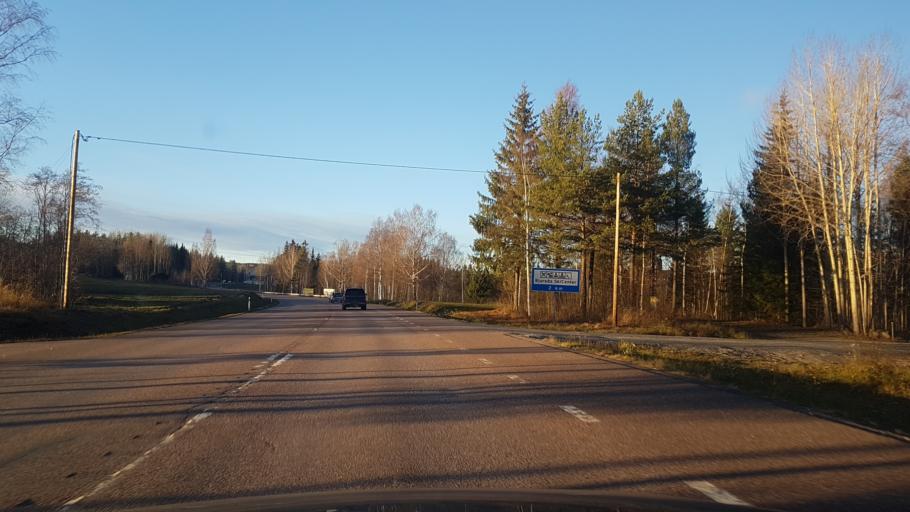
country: SE
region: Dalarna
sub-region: Faluns Kommun
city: Bjursas
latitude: 60.7185
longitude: 15.4574
